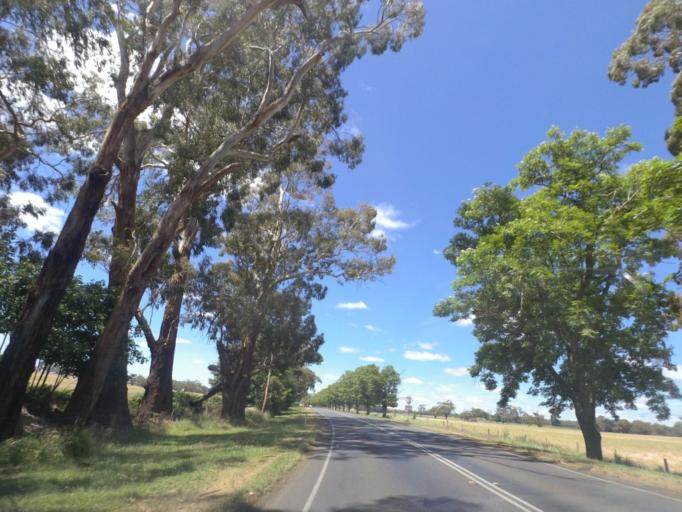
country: AU
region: Victoria
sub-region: Mount Alexander
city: Castlemaine
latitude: -37.3350
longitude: 144.1685
